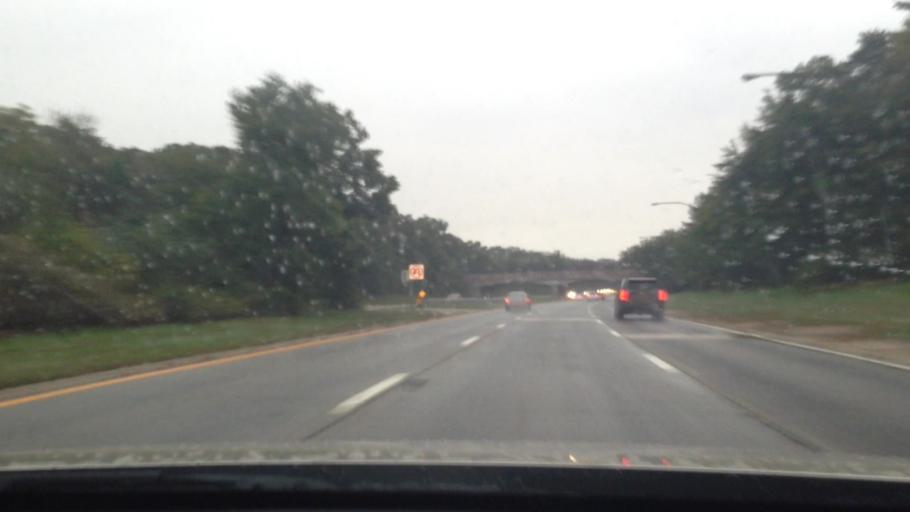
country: US
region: New York
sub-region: Suffolk County
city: North Bay Shore
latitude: 40.7510
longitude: -73.2458
